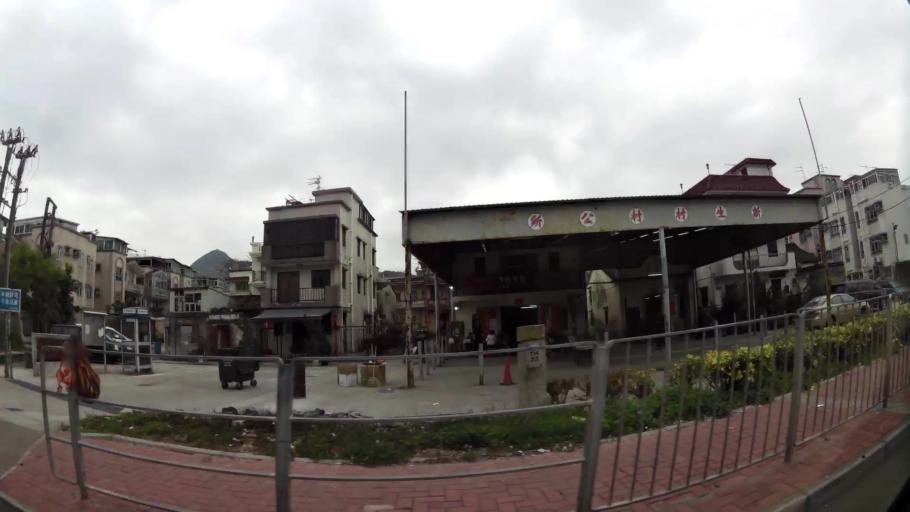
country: HK
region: Yuen Long
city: Yuen Long Kau Hui
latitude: 22.4399
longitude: 113.9916
